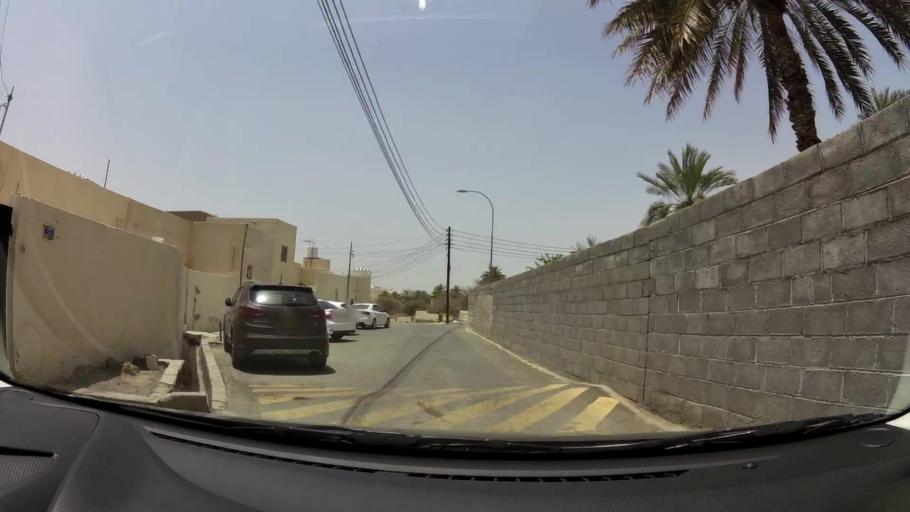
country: OM
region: Muhafazat Masqat
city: Bawshar
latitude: 23.5315
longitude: 58.3906
